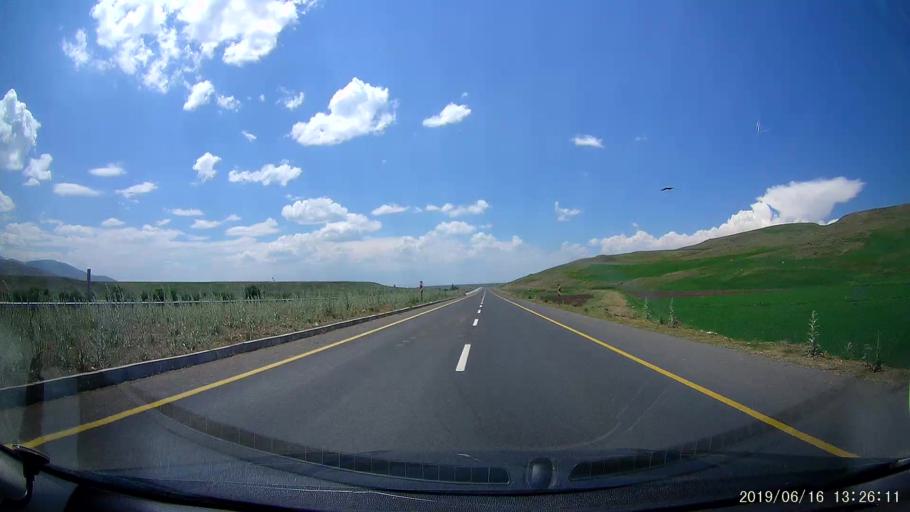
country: TR
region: Agri
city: Taslicay
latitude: 39.6575
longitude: 43.3341
